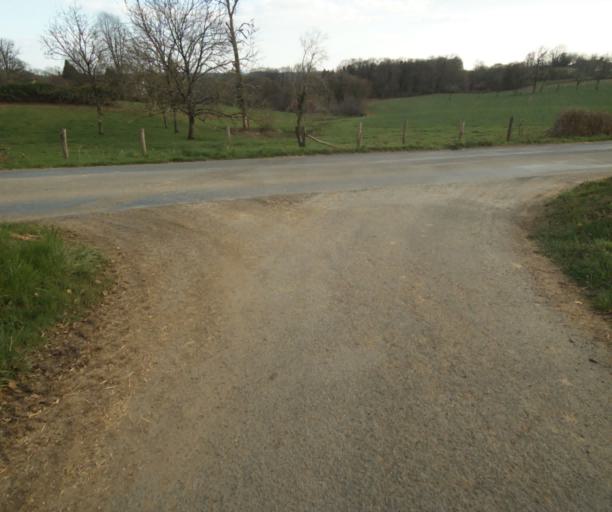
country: FR
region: Limousin
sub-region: Departement de la Correze
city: Saint-Clement
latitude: 45.3631
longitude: 1.6429
